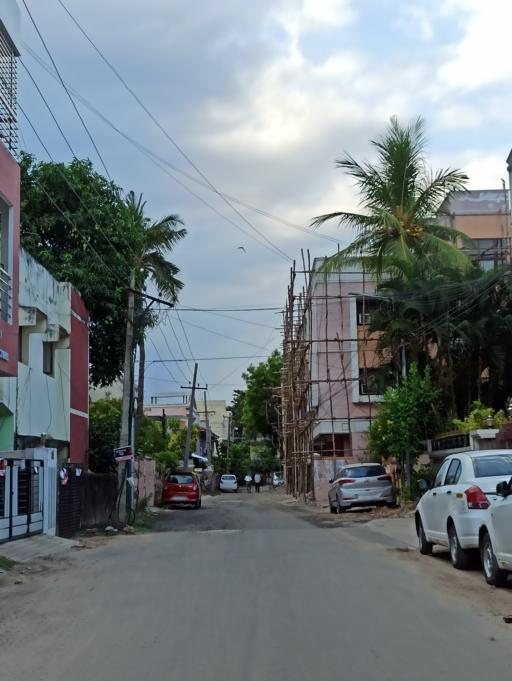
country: IN
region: Tamil Nadu
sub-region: Chennai
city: Chetput
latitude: 13.0583
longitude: 80.2066
